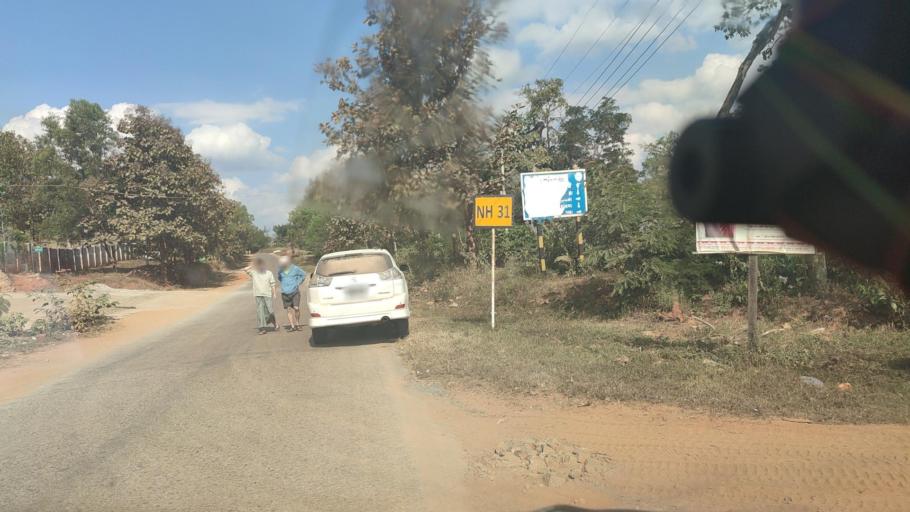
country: MM
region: Mandalay
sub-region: Pyin Oo Lwin District
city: Pyin Oo Lwin
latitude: 21.6227
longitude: 96.9238
